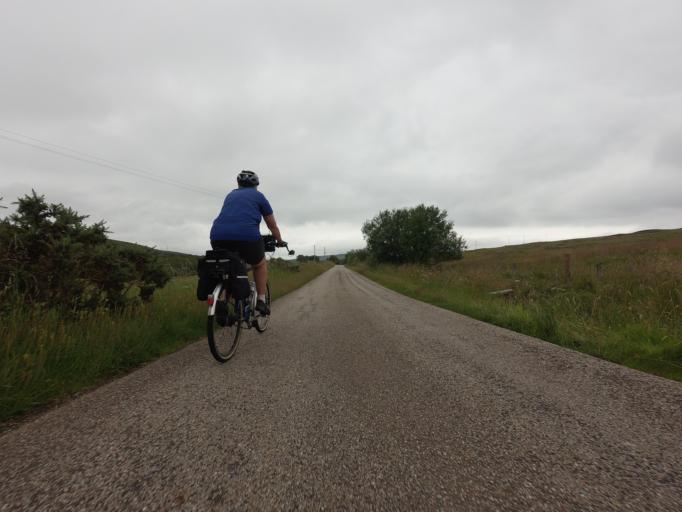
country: GB
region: Scotland
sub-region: Highland
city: Alness
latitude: 58.0077
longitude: -4.4042
